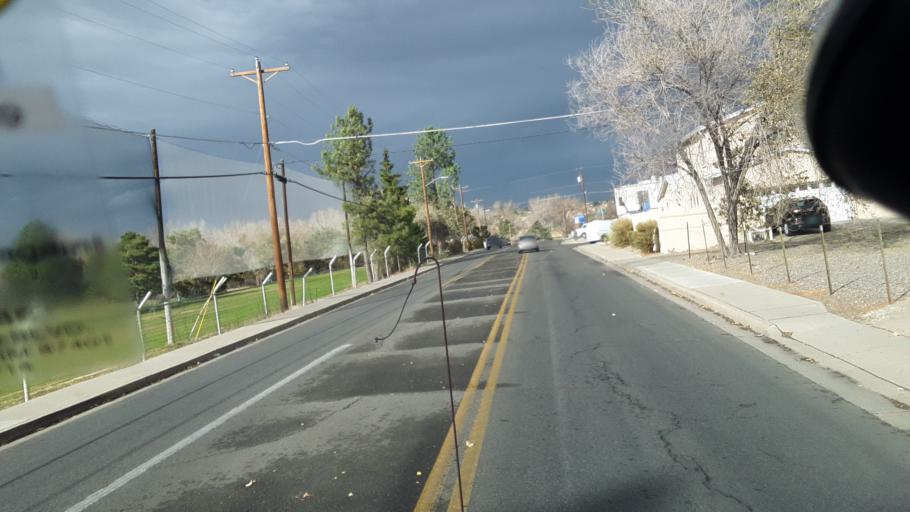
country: US
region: New Mexico
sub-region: San Juan County
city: Farmington
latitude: 36.7504
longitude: -108.1977
